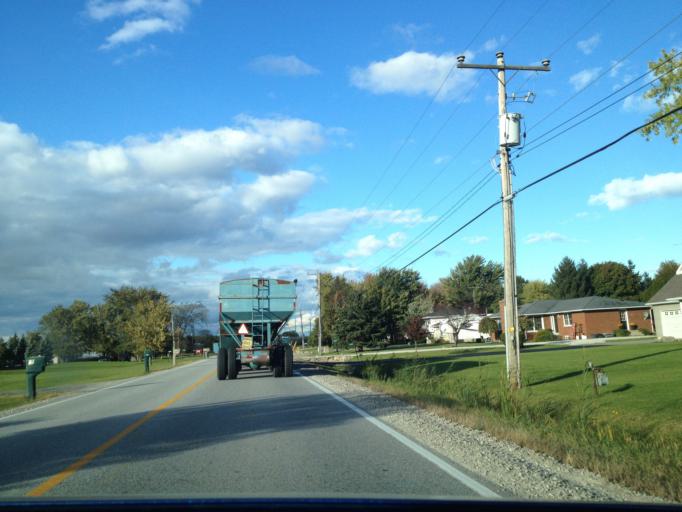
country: US
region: Michigan
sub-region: Wayne County
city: Grosse Pointe
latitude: 42.2331
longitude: -82.7132
